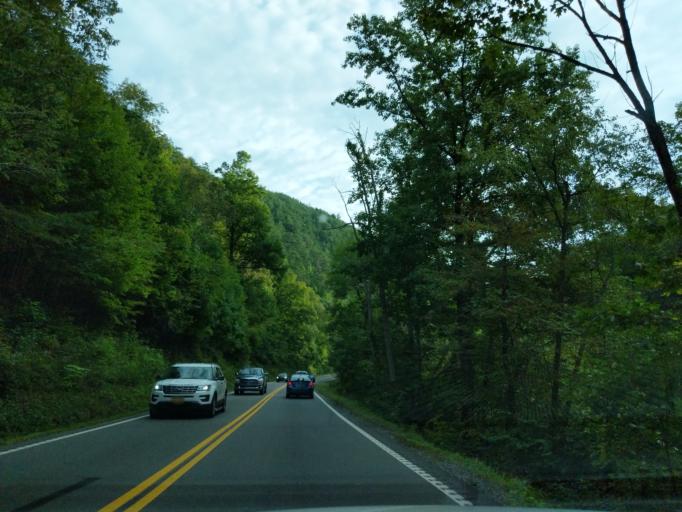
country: US
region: Georgia
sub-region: Fannin County
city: McCaysville
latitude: 35.0745
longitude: -84.5035
